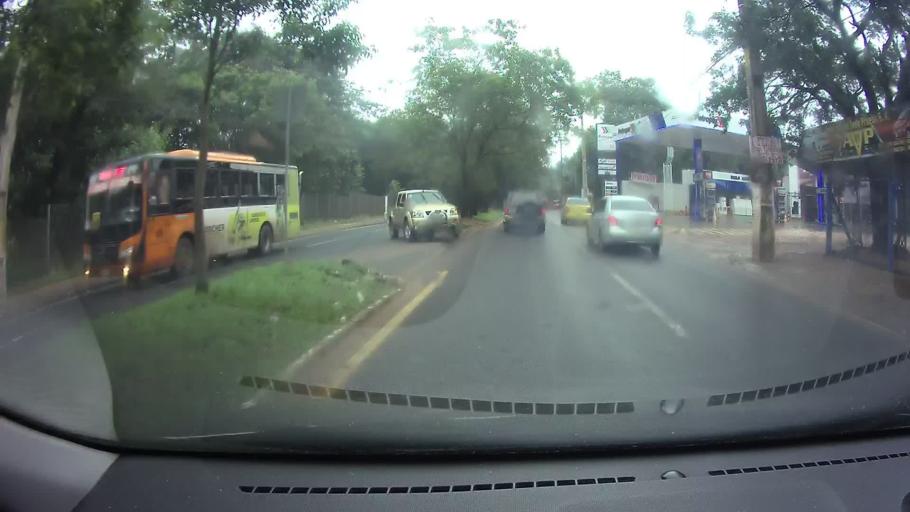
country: PY
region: Central
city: Fernando de la Mora
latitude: -25.3279
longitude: -57.5182
